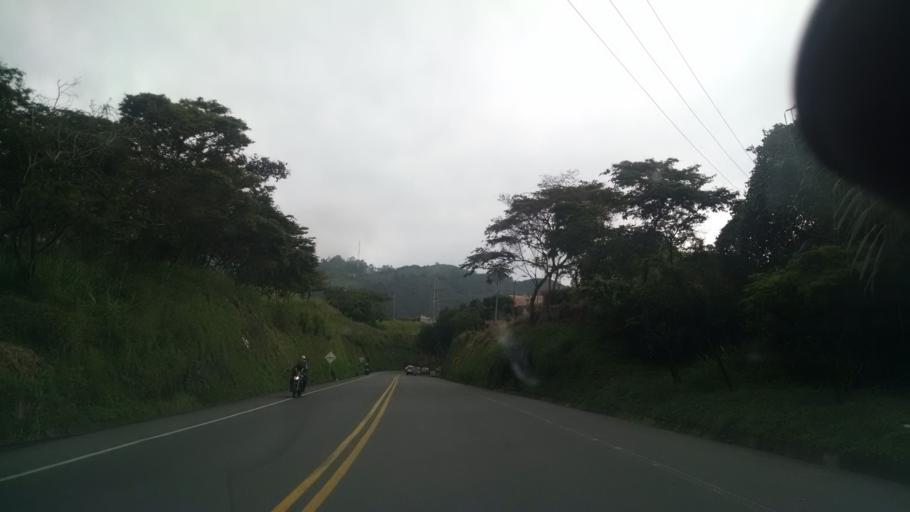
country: CO
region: Risaralda
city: Pereira
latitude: 4.8195
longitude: -75.7282
